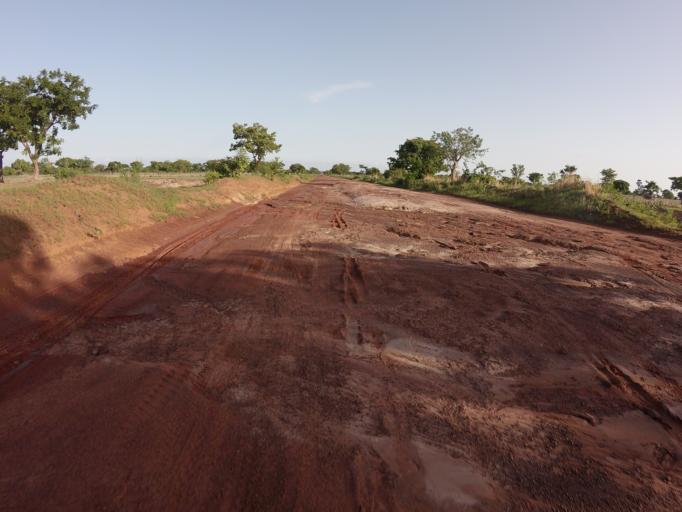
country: TG
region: Savanes
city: Sansanne-Mango
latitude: 10.3756
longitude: -0.0944
